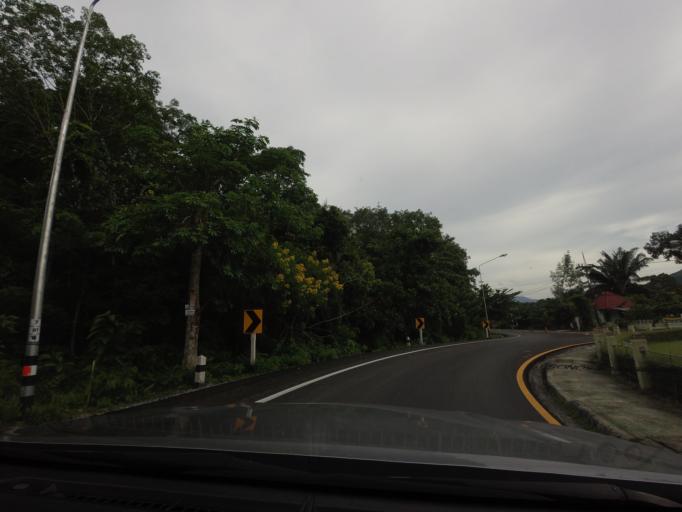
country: TH
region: Yala
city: Raman
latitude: 6.4444
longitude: 101.4515
